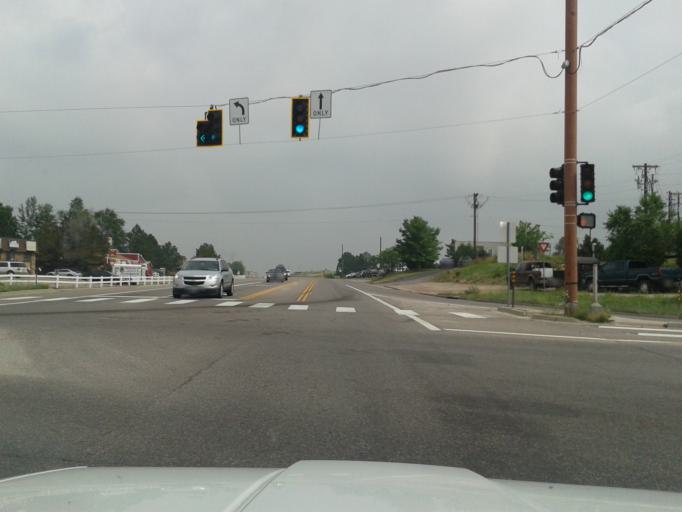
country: US
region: Colorado
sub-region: Douglas County
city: The Pinery
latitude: 39.3911
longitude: -104.7528
